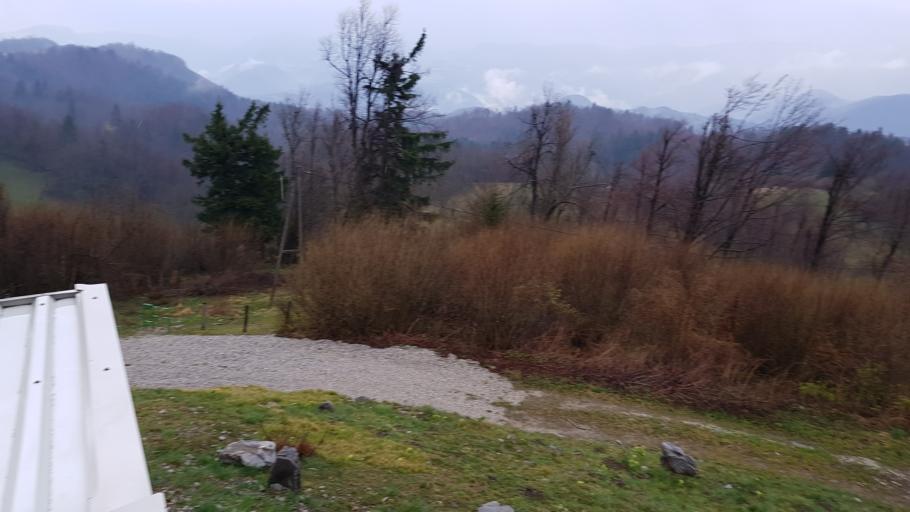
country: SI
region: Cerkno
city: Cerkno
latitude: 46.1430
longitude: 13.8649
